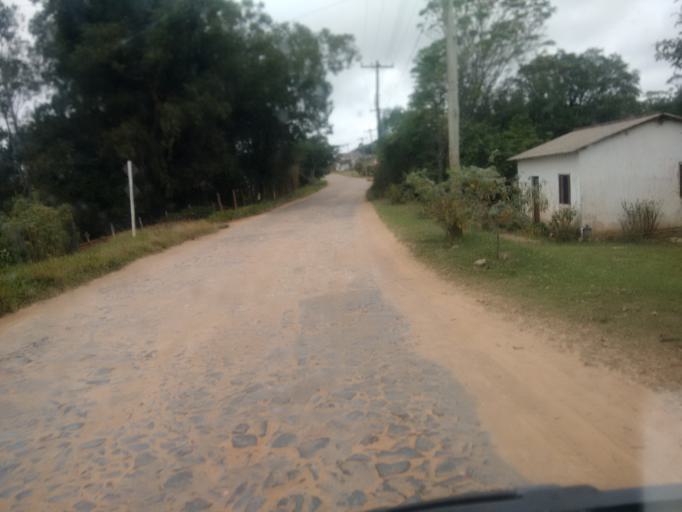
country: BR
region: Rio Grande do Sul
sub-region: Camaqua
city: Camaqua
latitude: -30.7941
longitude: -51.8306
